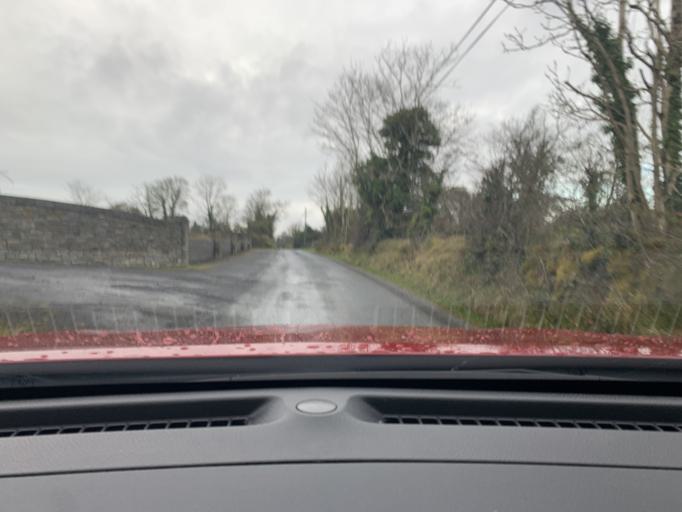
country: IE
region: Connaught
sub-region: Roscommon
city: Ballaghaderreen
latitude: 53.9662
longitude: -8.5566
